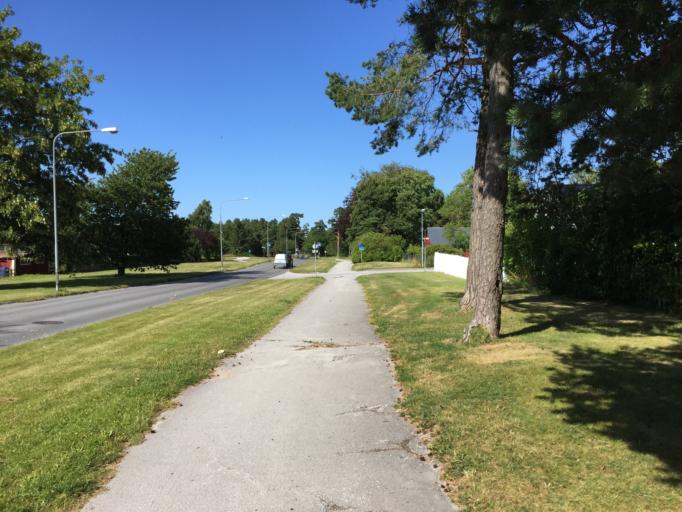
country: SE
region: Gotland
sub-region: Gotland
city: Visby
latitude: 57.6129
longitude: 18.2948
